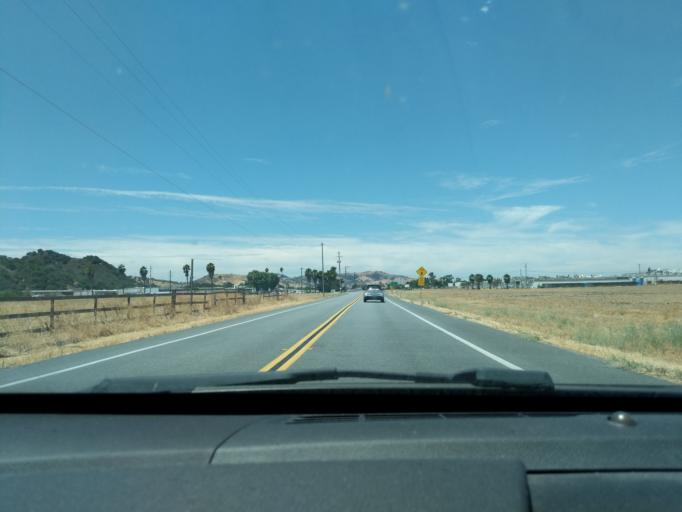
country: US
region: California
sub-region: Santa Clara County
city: Morgan Hill
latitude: 37.1629
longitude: -121.7013
